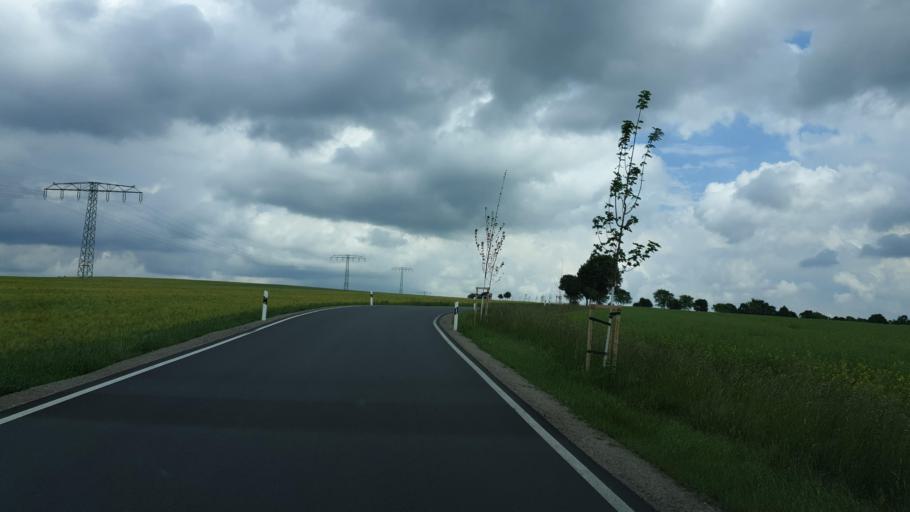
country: DE
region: Saxony
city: Marienberg
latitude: 50.6723
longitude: 13.1481
